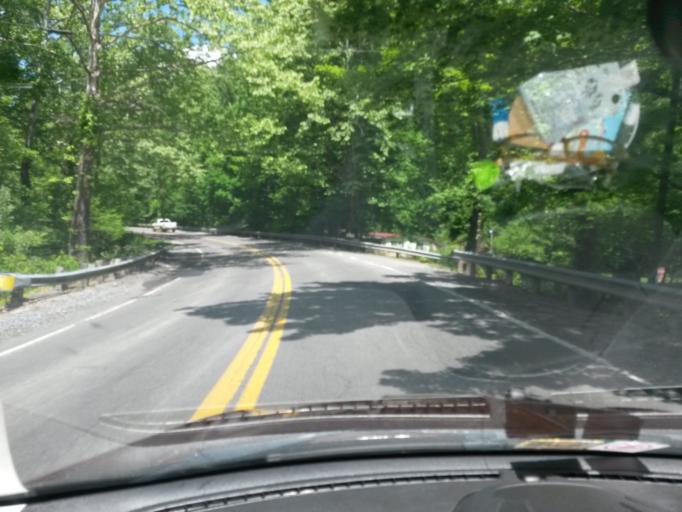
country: US
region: West Virginia
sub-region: Wyoming County
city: Pineville
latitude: 37.5157
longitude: -81.5806
